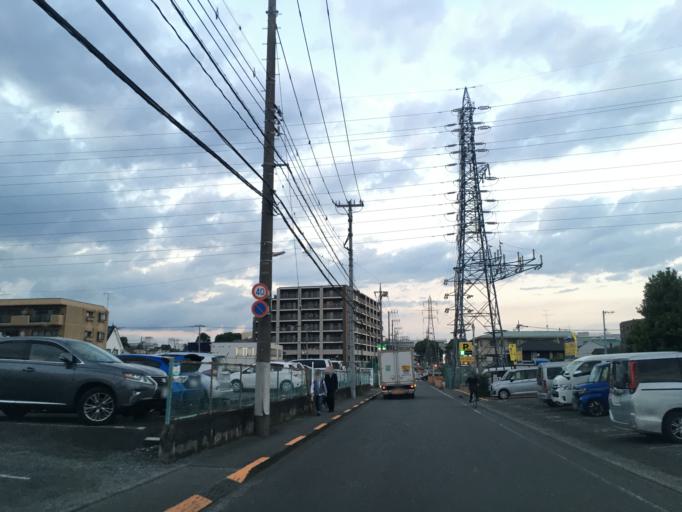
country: JP
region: Tokyo
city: Higashimurayama-shi
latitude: 35.7311
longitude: 139.4711
